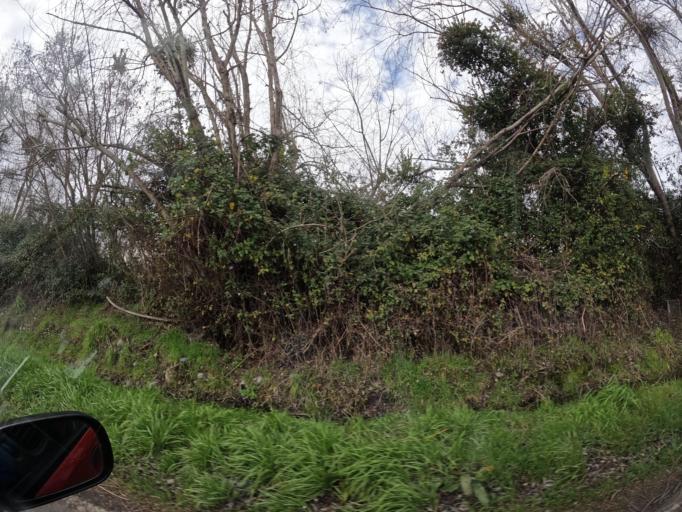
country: CL
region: Maule
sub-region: Provincia de Linares
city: Linares
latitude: -35.8613
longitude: -71.6168
